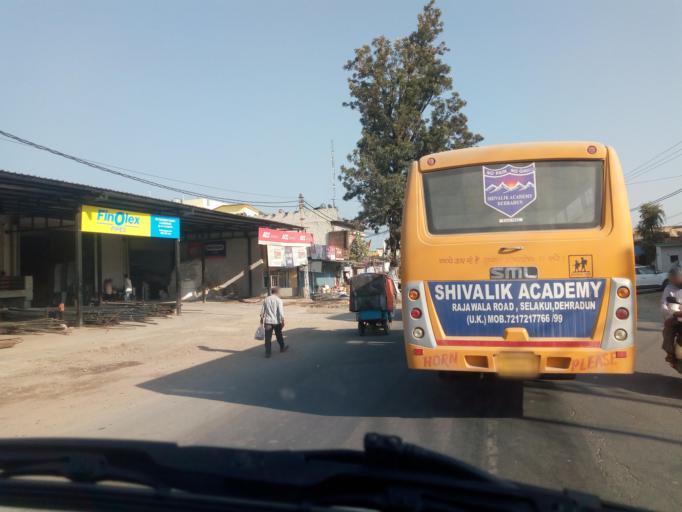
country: IN
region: Uttarakhand
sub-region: Dehradun
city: Vikasnagar
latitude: 30.3539
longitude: 77.8583
